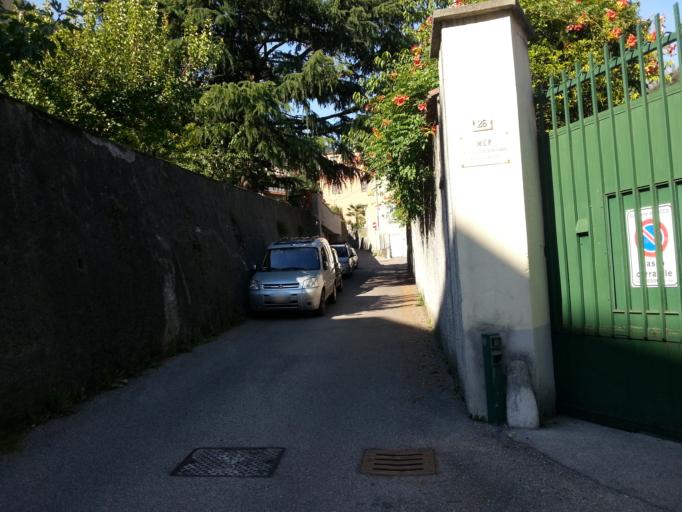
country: IT
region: Lombardy
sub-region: Provincia di Lecco
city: Ballabio
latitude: 45.8765
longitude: 9.4045
